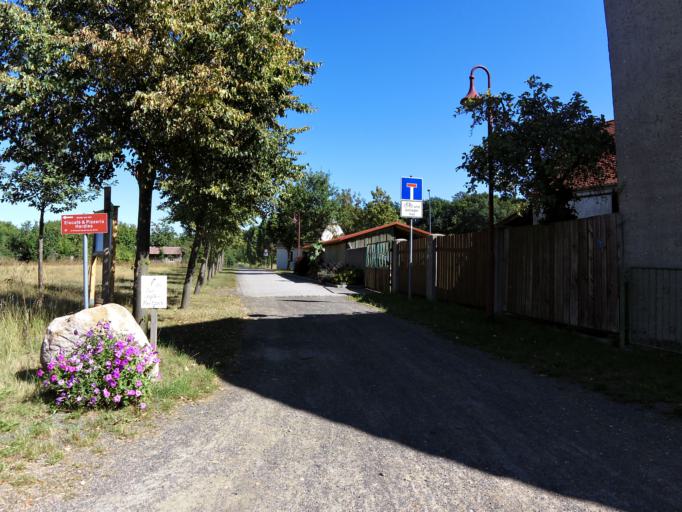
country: DE
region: Saxony-Anhalt
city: Pretzsch
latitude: 51.6874
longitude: 12.8268
